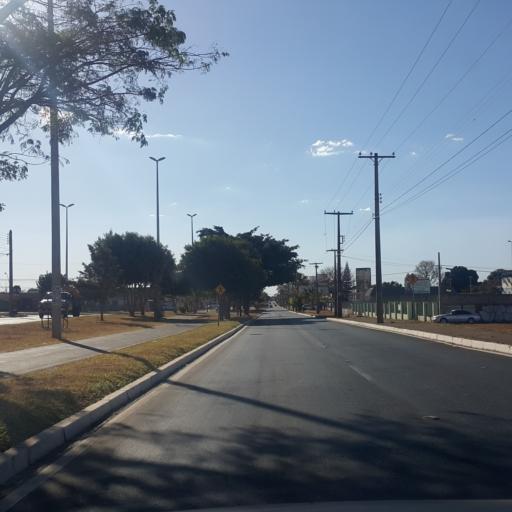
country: BR
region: Federal District
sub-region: Brasilia
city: Brasilia
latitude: -15.8071
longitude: -48.1027
